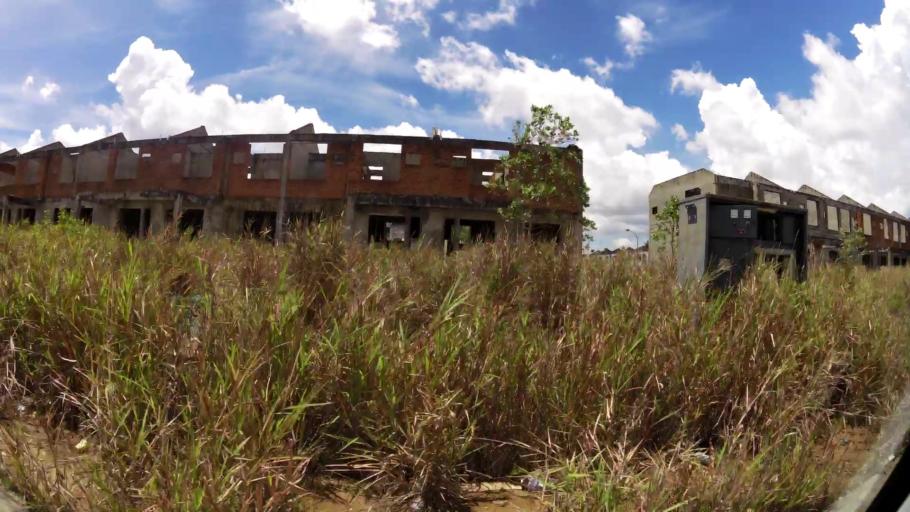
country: BN
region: Brunei and Muara
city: Bandar Seri Begawan
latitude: 4.9692
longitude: 114.9110
